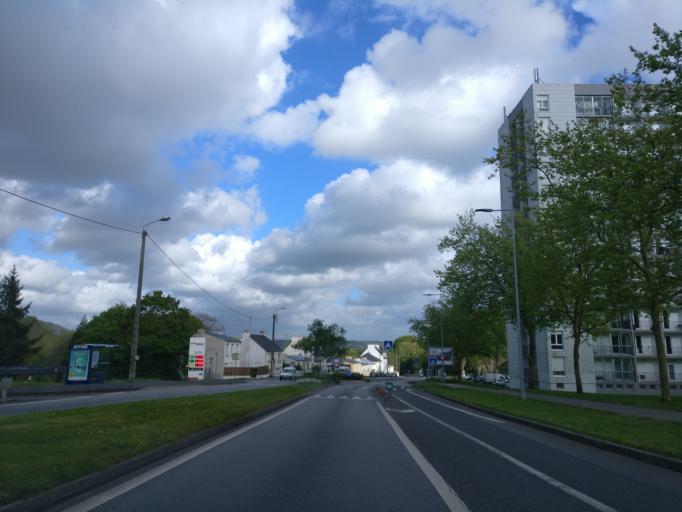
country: FR
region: Brittany
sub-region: Departement du Finistere
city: Brest
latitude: 48.4012
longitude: -4.4467
